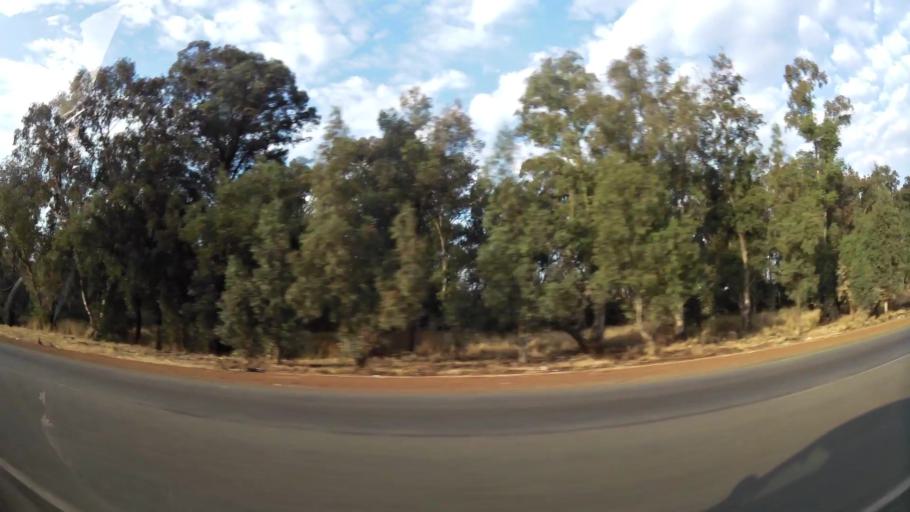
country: ZA
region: Gauteng
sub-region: Sedibeng District Municipality
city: Vanderbijlpark
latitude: -26.7126
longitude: 27.8173
